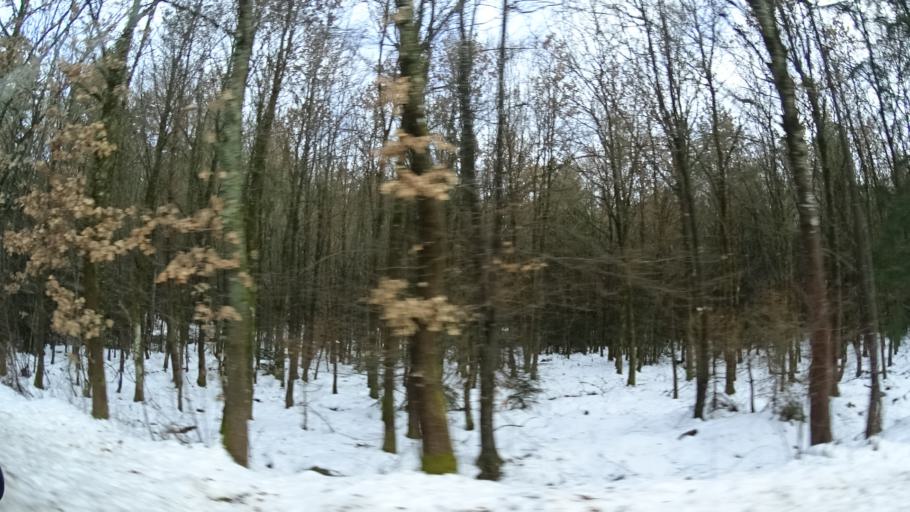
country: DE
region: Baden-Wuerttemberg
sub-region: Karlsruhe Region
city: Fahrenbach
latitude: 49.4842
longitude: 9.1536
